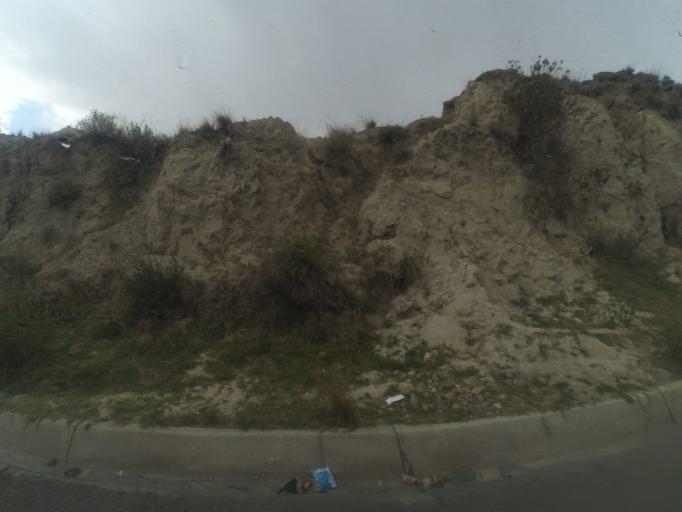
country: BO
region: La Paz
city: La Paz
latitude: -16.5657
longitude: -68.1733
